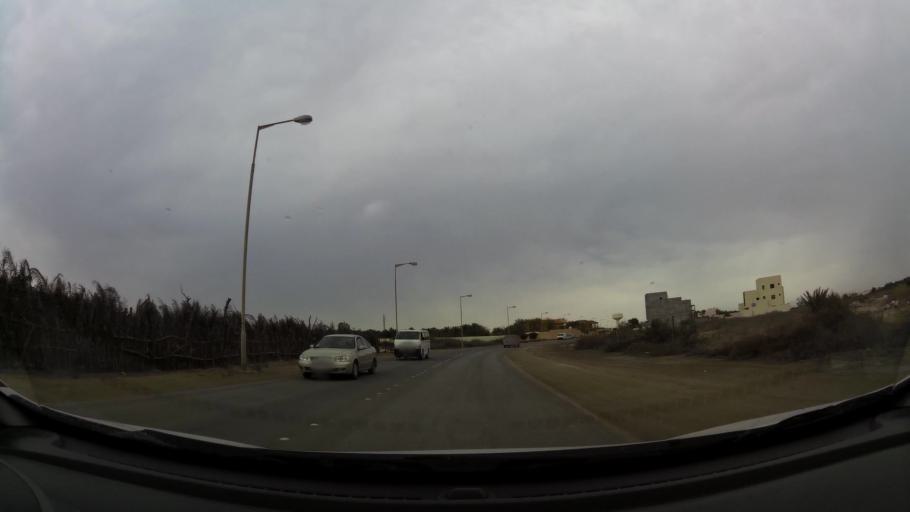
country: BH
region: Central Governorate
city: Madinat Hamad
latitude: 26.1341
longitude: 50.4657
